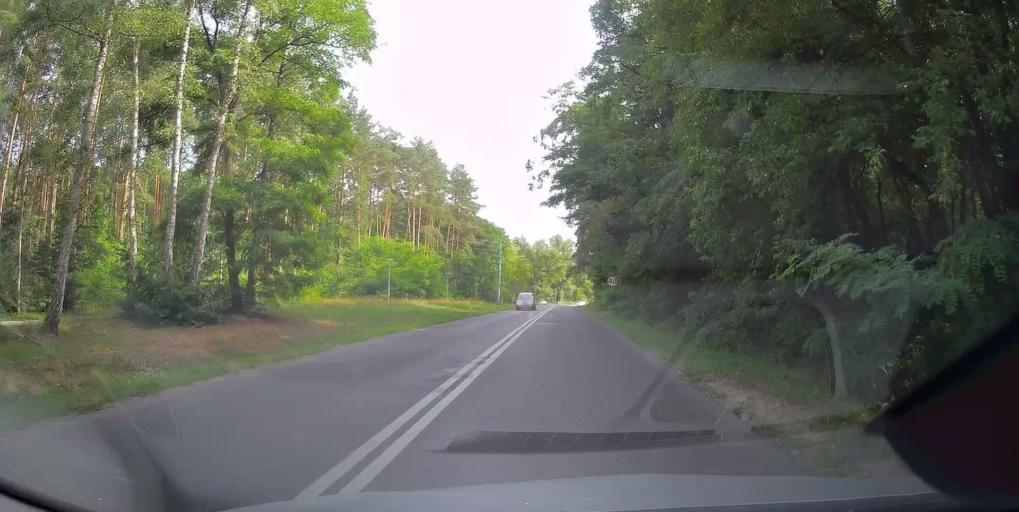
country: PL
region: Lodz Voivodeship
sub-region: Powiat tomaszowski
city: Tomaszow Mazowiecki
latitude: 51.5013
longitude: 19.9953
